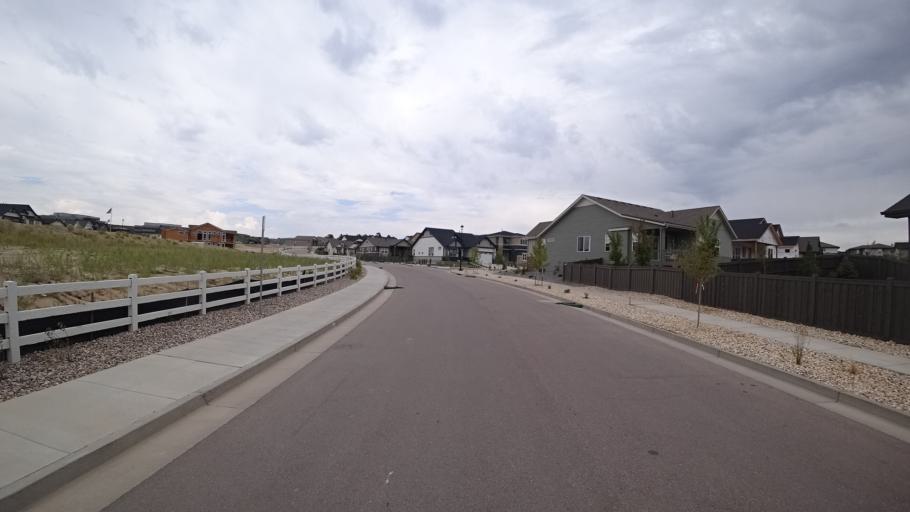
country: US
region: Colorado
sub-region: El Paso County
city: Gleneagle
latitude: 39.0050
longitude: -104.8111
